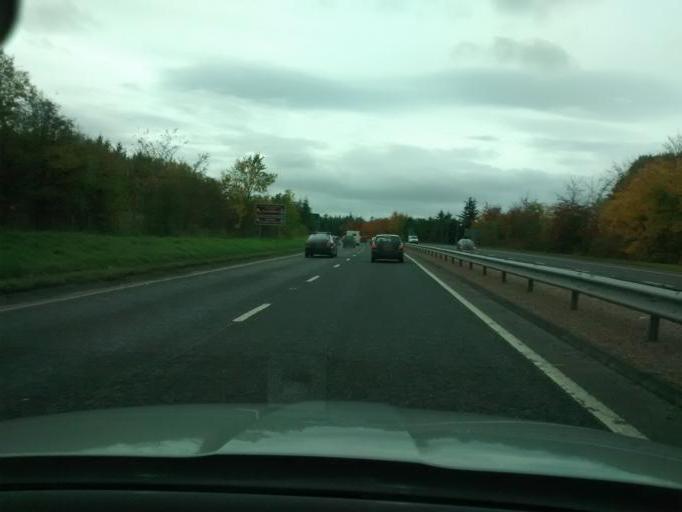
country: GB
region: Scotland
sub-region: Perth and Kinross
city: Luncarty
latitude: 56.4150
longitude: -3.4744
